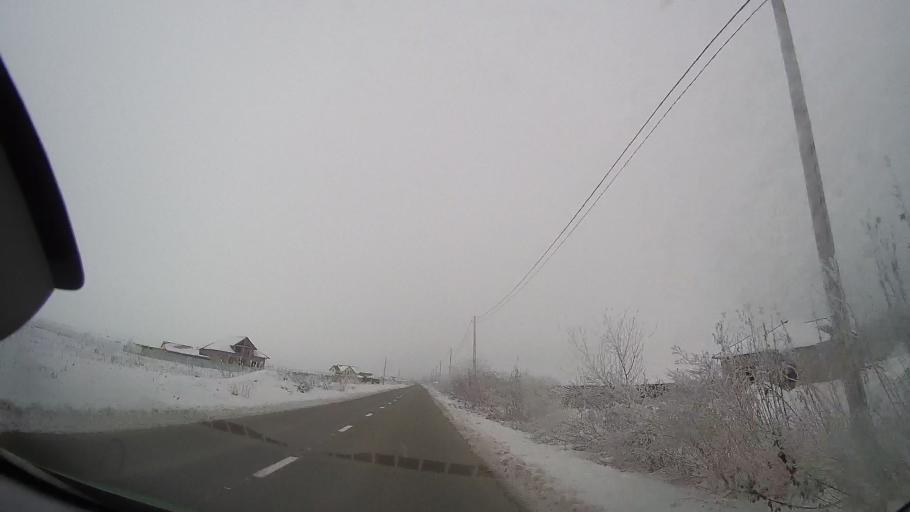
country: RO
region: Neamt
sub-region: Comuna Horia
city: Cotu Vames
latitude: 46.8912
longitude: 26.9643
